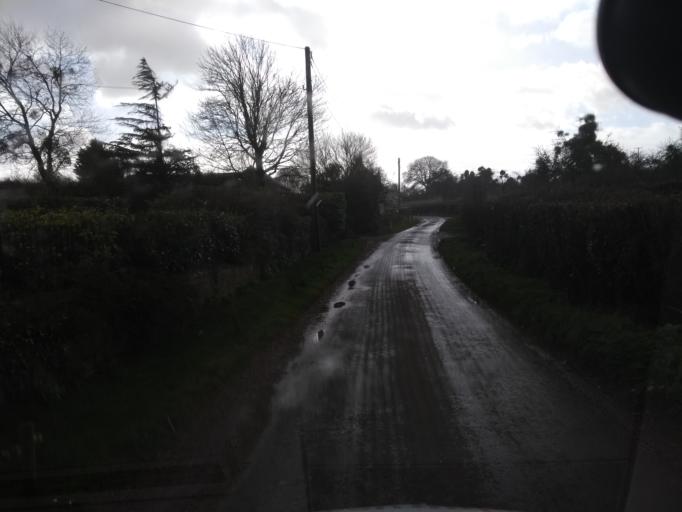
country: GB
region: England
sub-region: Somerset
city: South Petherton
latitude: 50.9716
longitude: -2.8107
